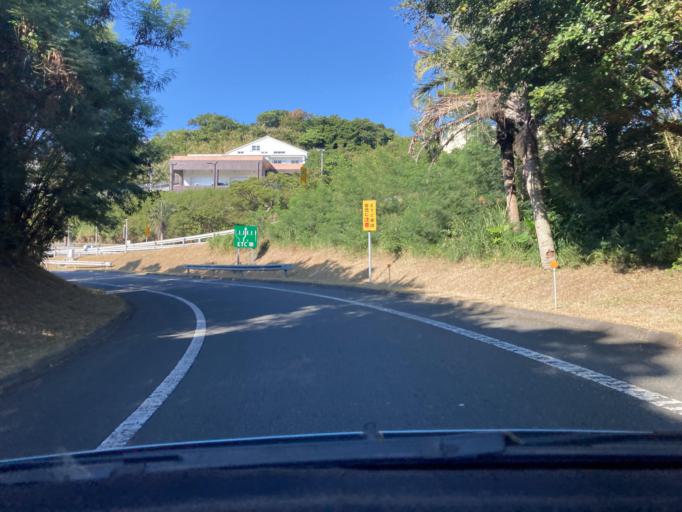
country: JP
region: Okinawa
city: Ginowan
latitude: 26.2480
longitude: 127.7498
